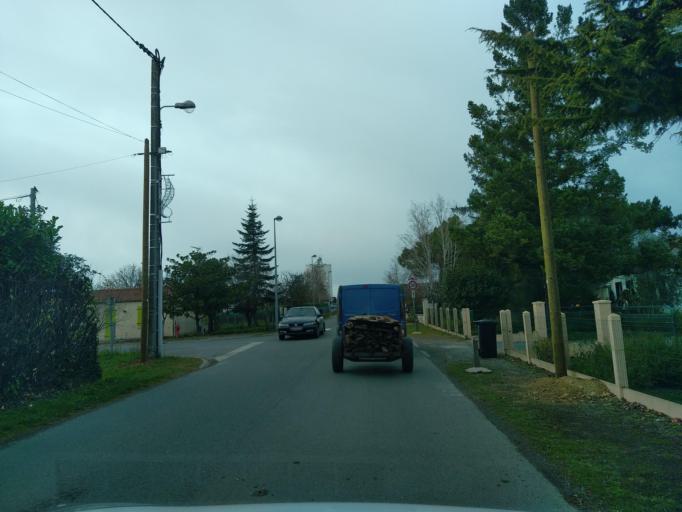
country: FR
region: Pays de la Loire
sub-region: Departement de la Vendee
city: Vix
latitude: 46.3675
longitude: -0.8662
